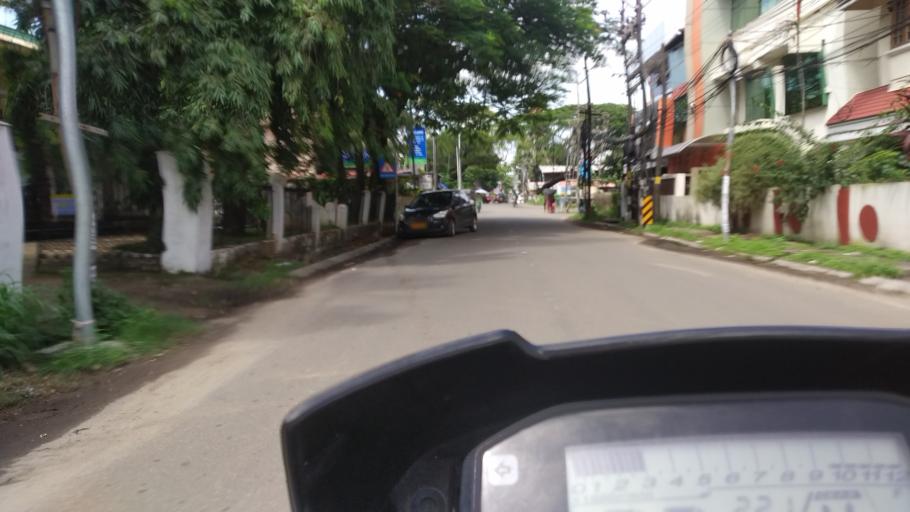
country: IN
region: Kerala
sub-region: Ernakulam
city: Cochin
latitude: 9.9652
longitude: 76.2970
